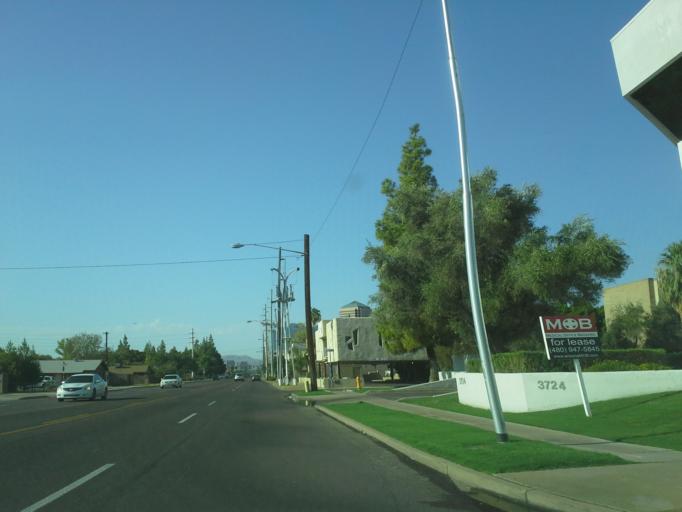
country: US
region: Arizona
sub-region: Maricopa County
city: Phoenix
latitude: 33.4909
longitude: -112.0695
